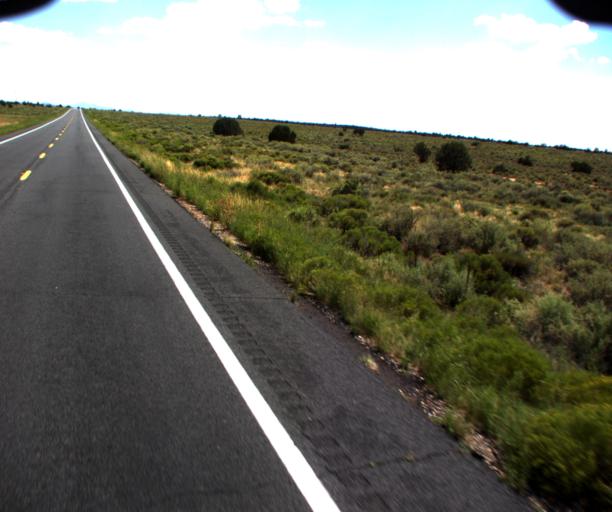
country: US
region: Arizona
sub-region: Coconino County
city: Grand Canyon Village
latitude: 35.6992
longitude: -112.1331
